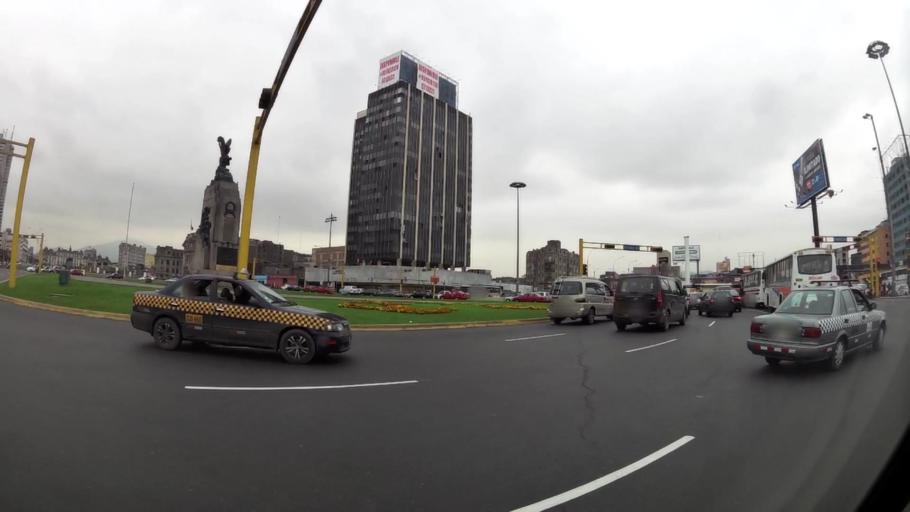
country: PE
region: Lima
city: Lima
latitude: -12.0603
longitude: -77.0359
